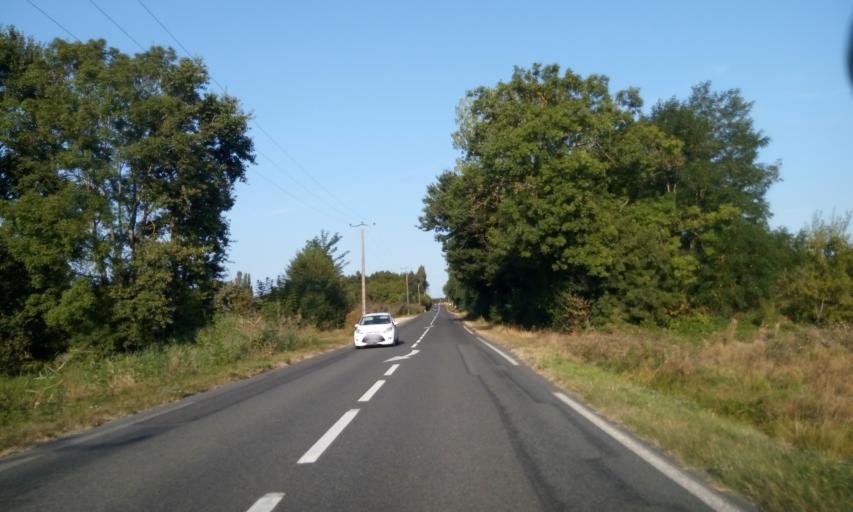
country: FR
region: Rhone-Alpes
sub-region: Departement de l'Ain
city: Villars-les-Dombes
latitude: 45.9851
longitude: 4.9832
